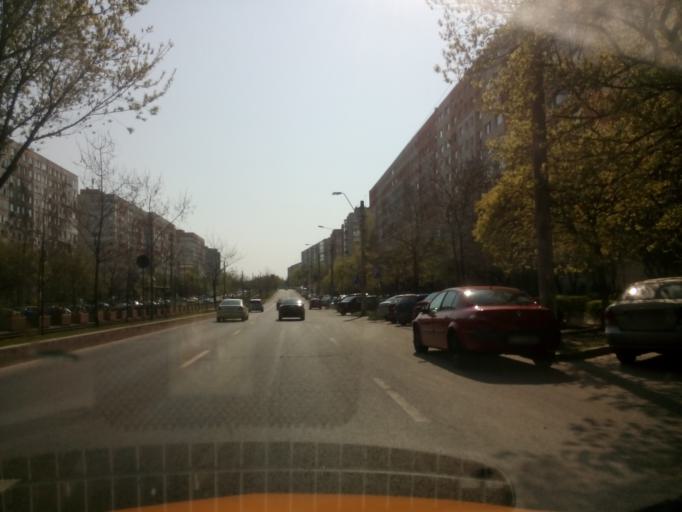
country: RO
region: Ilfov
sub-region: Comuna Popesti-Leordeni
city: Popesti-Leordeni
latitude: 44.4124
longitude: 26.1663
